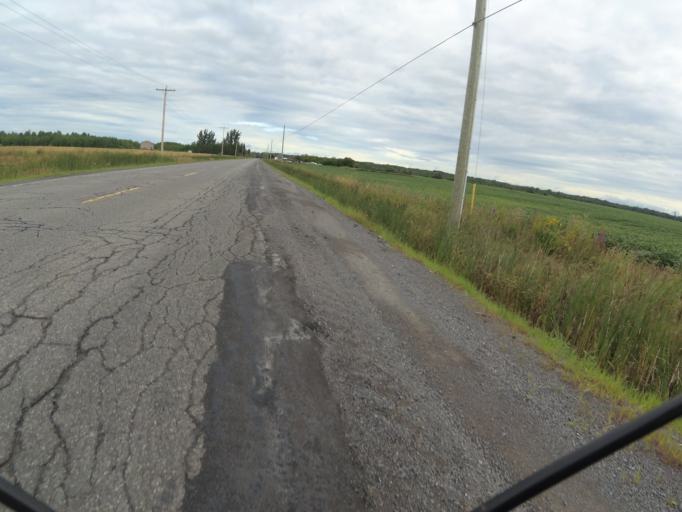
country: CA
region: Ontario
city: Bourget
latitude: 45.3799
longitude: -75.2727
